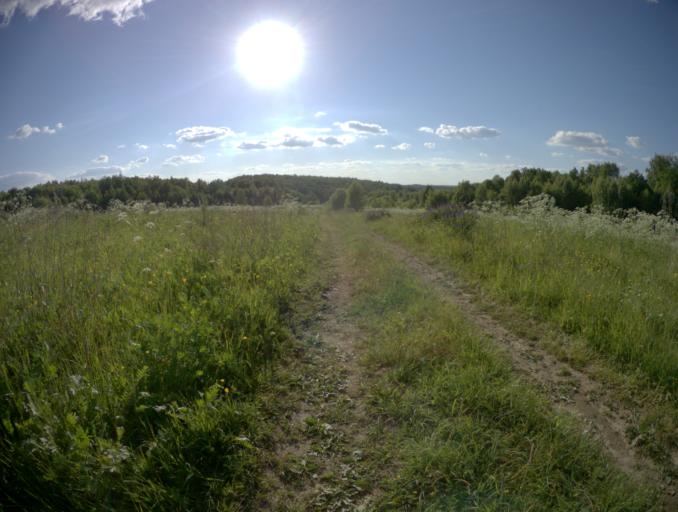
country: RU
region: Vladimir
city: Stavrovo
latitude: 56.2452
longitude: 40.0884
